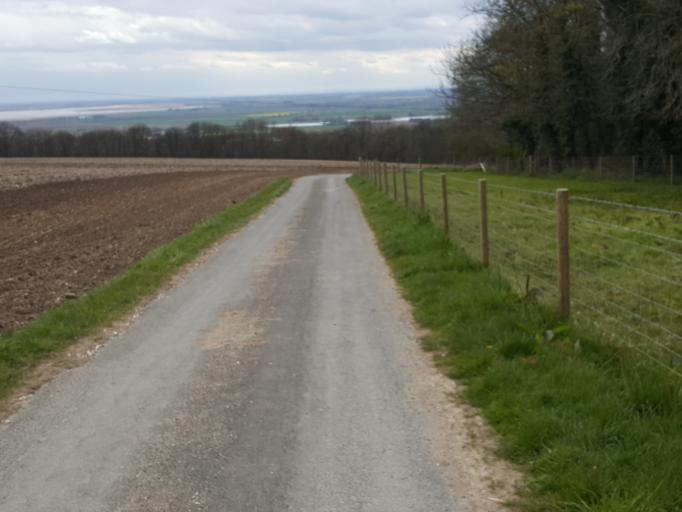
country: GB
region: England
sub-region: East Riding of Yorkshire
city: South Cave
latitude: 53.7682
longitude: -0.5841
